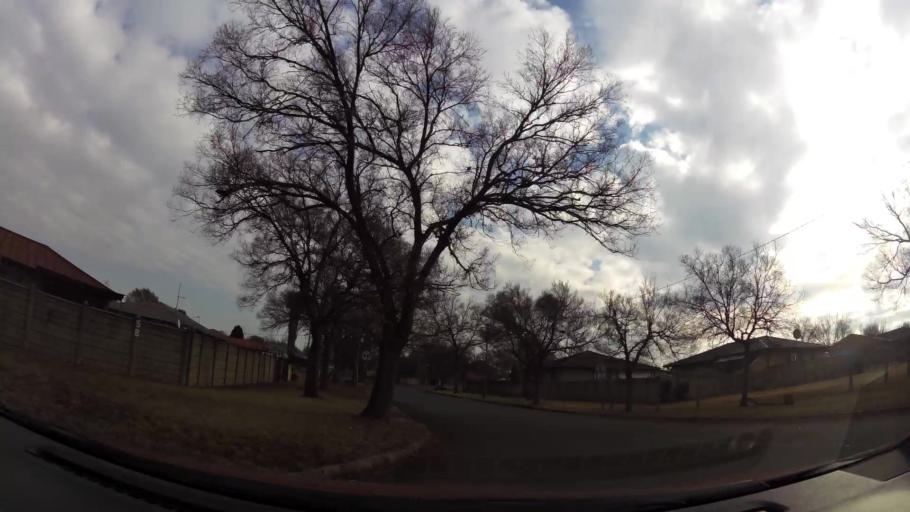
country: ZA
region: Gauteng
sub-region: Sedibeng District Municipality
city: Vanderbijlpark
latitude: -26.6956
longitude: 27.8143
